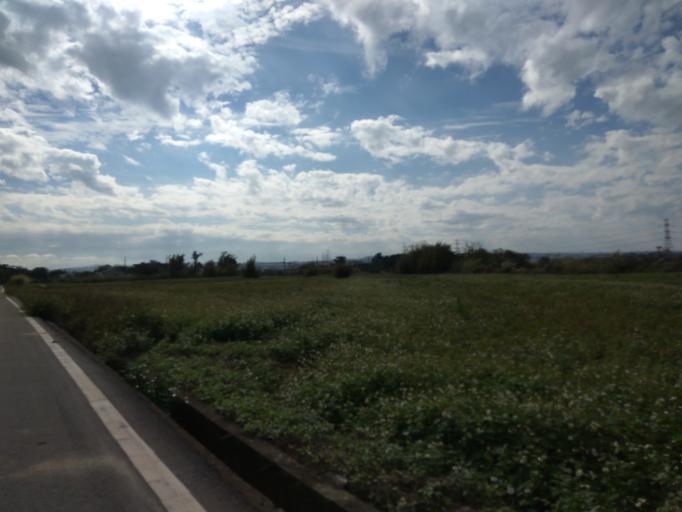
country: TW
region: Taiwan
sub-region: Hsinchu
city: Zhubei
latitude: 24.9587
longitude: 121.1043
